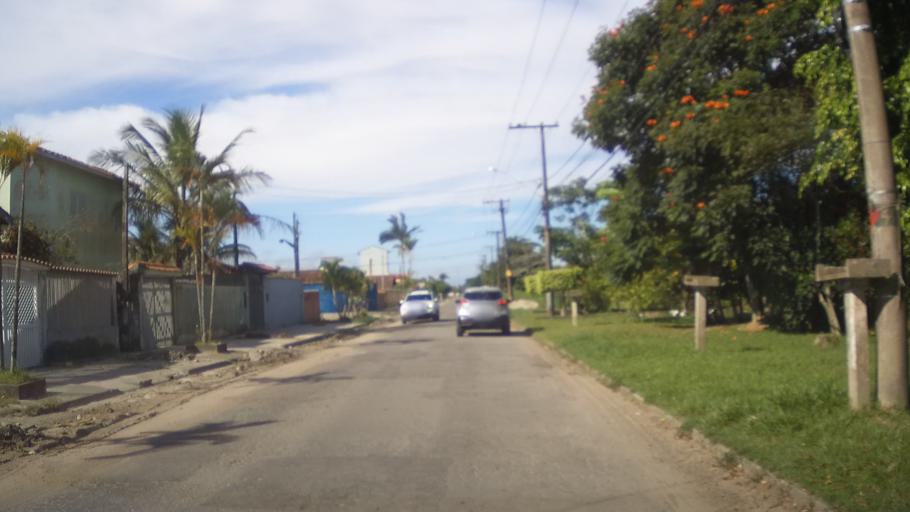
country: BR
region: Sao Paulo
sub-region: Itanhaem
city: Itanhaem
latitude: -24.2053
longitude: -46.8334
